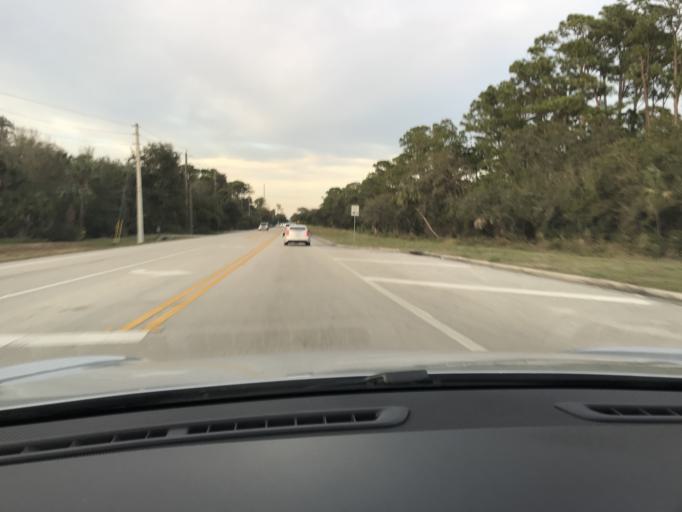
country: US
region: Florida
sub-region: Indian River County
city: Vero Beach South
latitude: 27.5947
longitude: -80.4306
